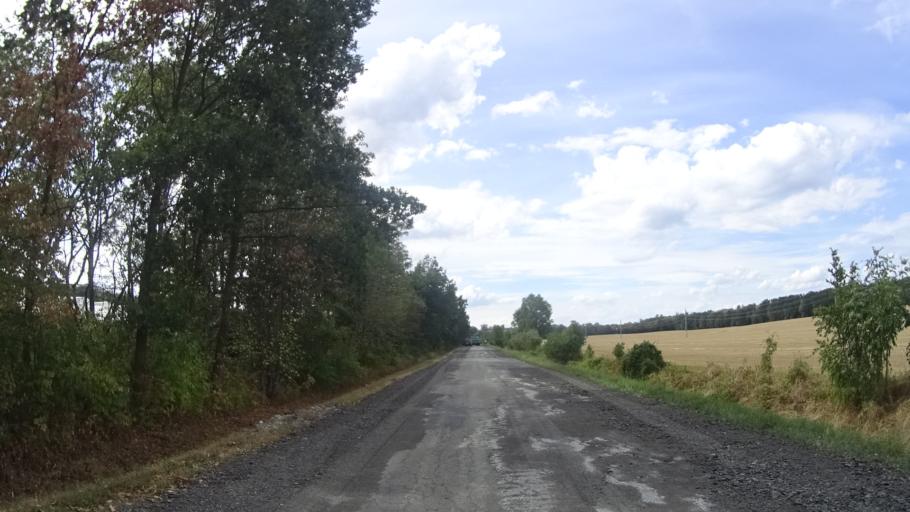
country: CZ
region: Olomoucky
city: Cervenka
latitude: 49.7174
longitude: 17.0435
